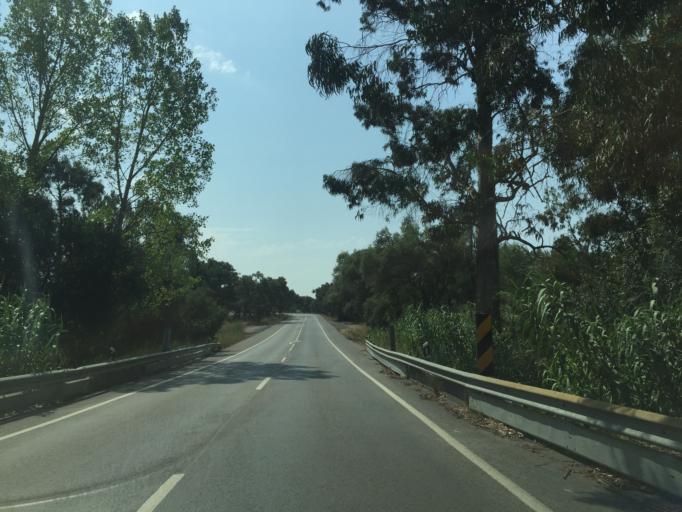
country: PT
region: Setubal
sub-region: Alcacer do Sal
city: Alcacer do Sal
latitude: 38.5488
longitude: -8.6489
